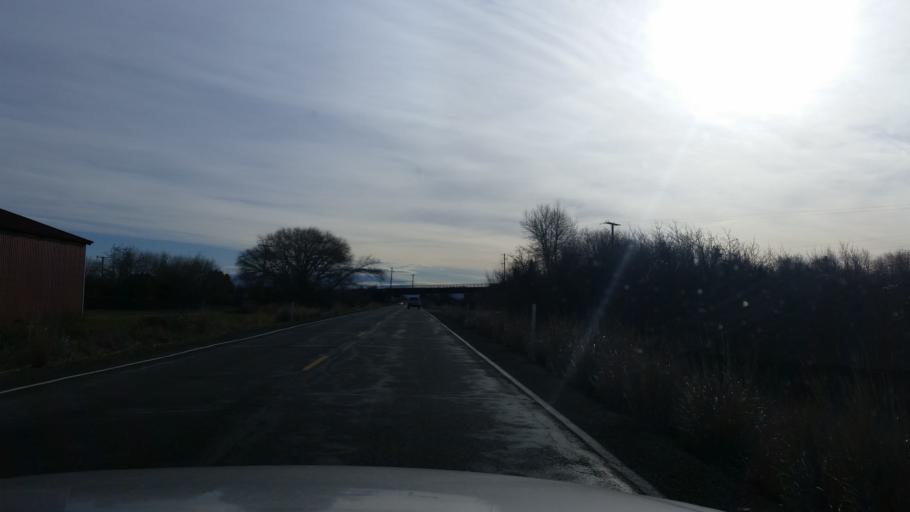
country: US
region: Washington
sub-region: Kittitas County
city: Ellensburg
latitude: 47.0438
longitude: -120.6244
